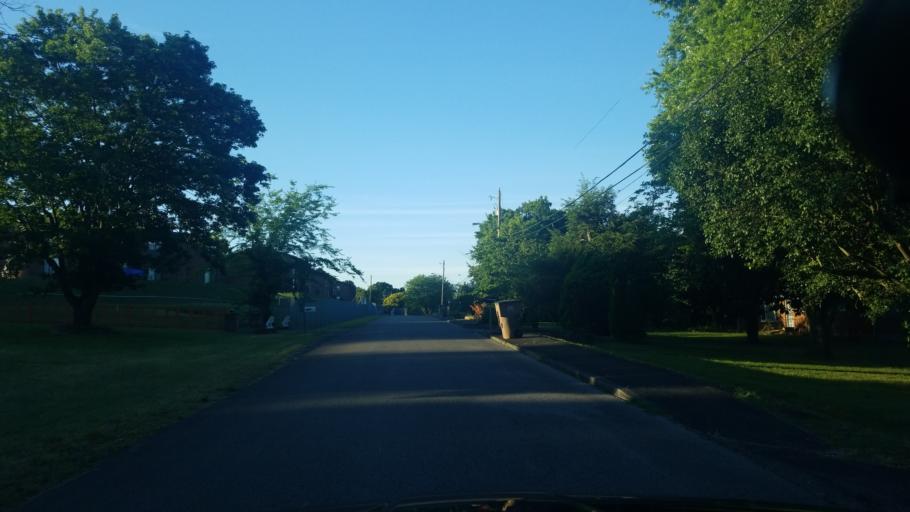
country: US
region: Tennessee
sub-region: Davidson County
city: Nashville
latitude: 36.2253
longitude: -86.7654
